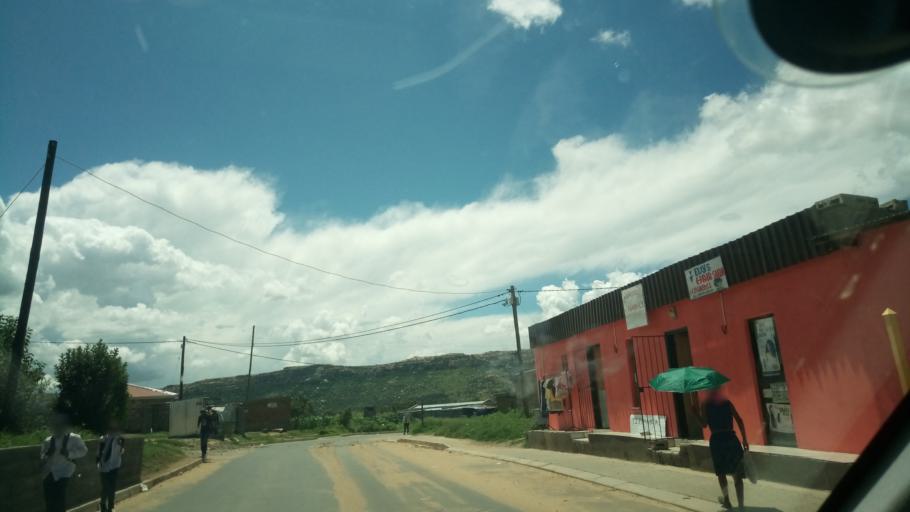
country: LS
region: Maseru
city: Maseru
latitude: -29.3668
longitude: 27.5404
